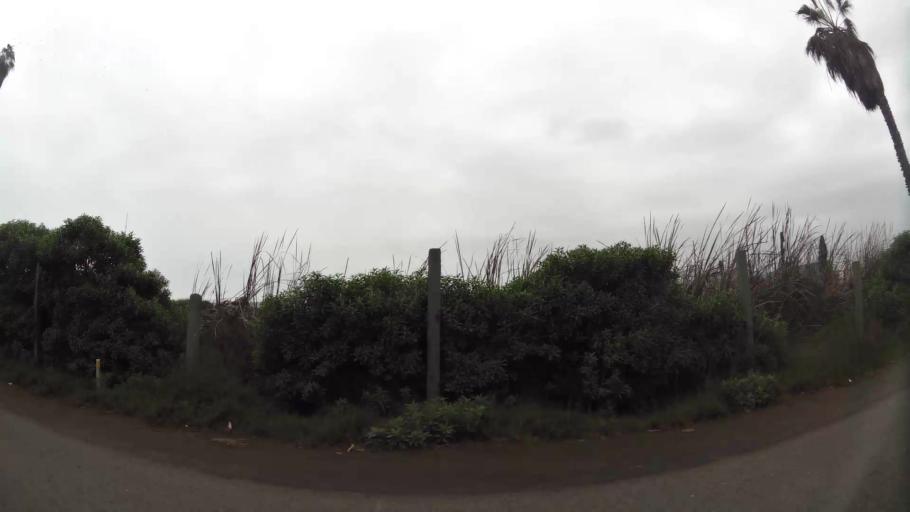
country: PE
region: Lima
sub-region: Lima
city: Surco
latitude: -12.2110
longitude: -76.9893
